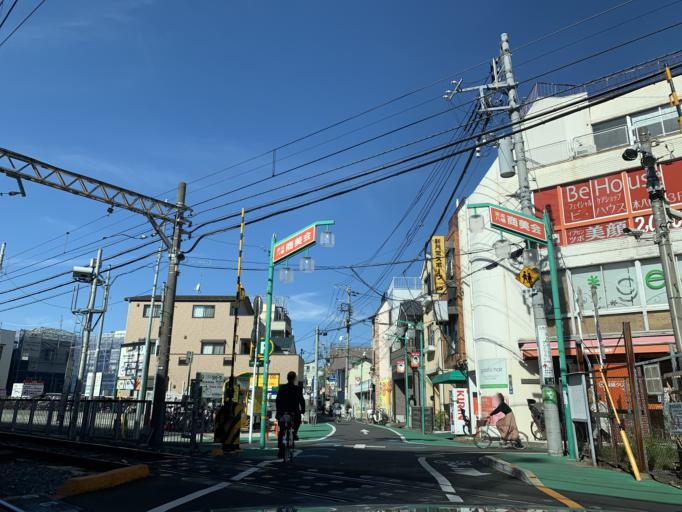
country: JP
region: Chiba
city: Funabashi
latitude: 35.7243
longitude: 139.9274
